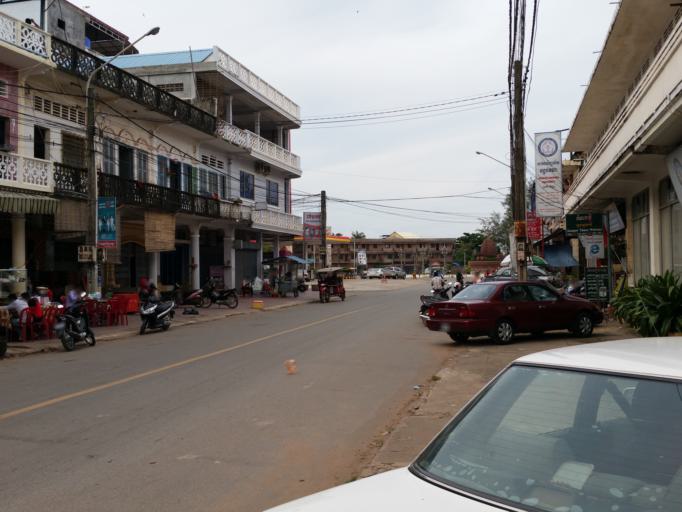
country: KH
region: Kampot
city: Kampot
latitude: 10.6100
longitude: 104.1803
